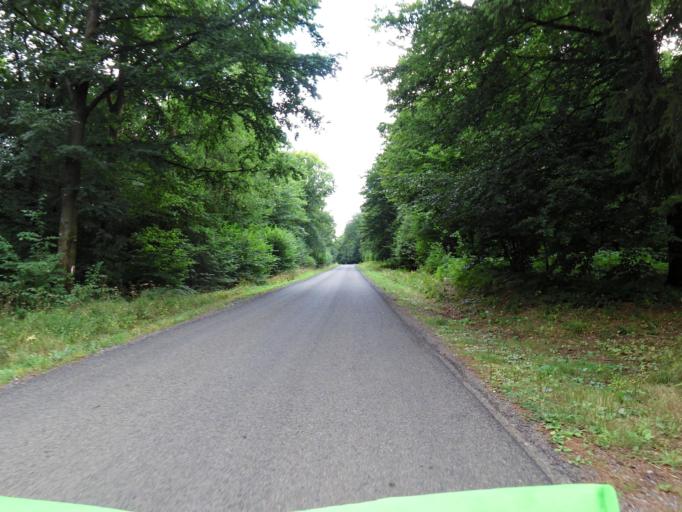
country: BE
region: Wallonia
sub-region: Province de Namur
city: Bievre
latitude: 49.9246
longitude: 5.0071
